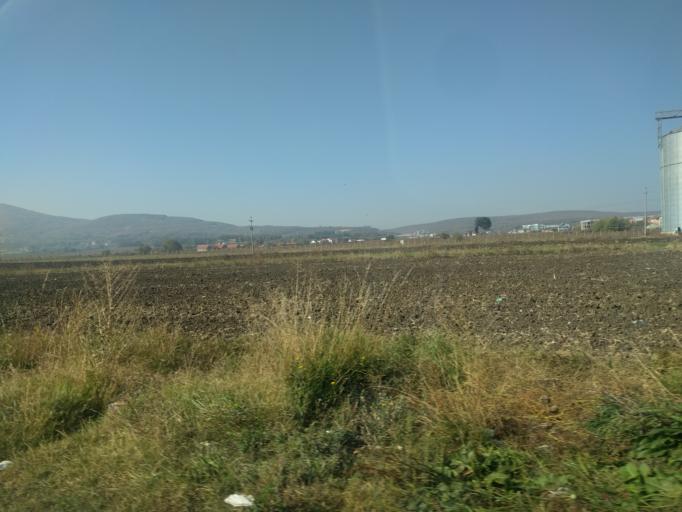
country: XK
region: Pristina
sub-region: Komuna e Gracanices
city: Glanica
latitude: 42.5955
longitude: 21.0194
